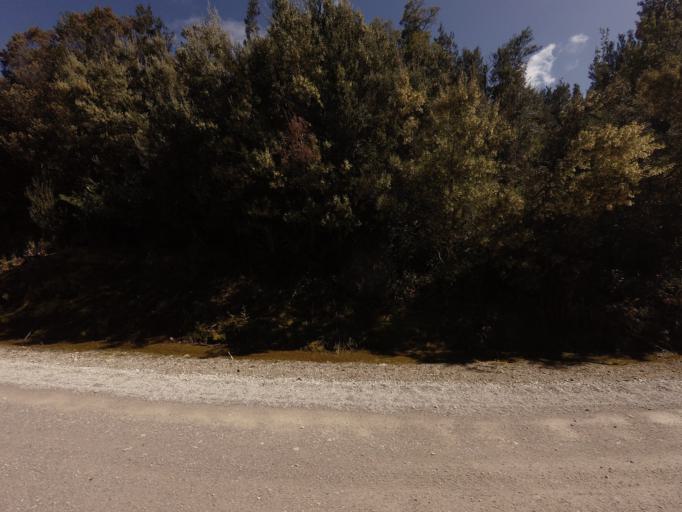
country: AU
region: Tasmania
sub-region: Huon Valley
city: Geeveston
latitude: -42.8345
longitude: 146.3816
